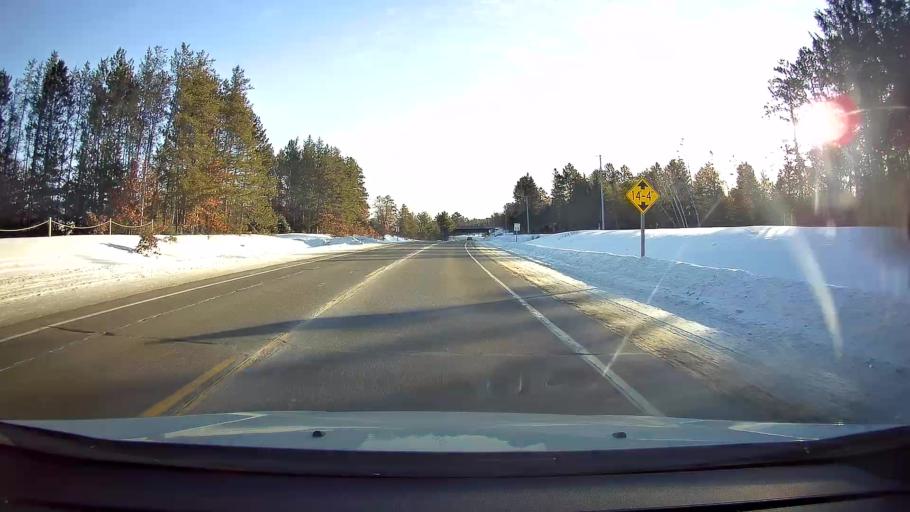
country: US
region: Wisconsin
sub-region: Washburn County
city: Spooner
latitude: 45.9055
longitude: -91.8218
